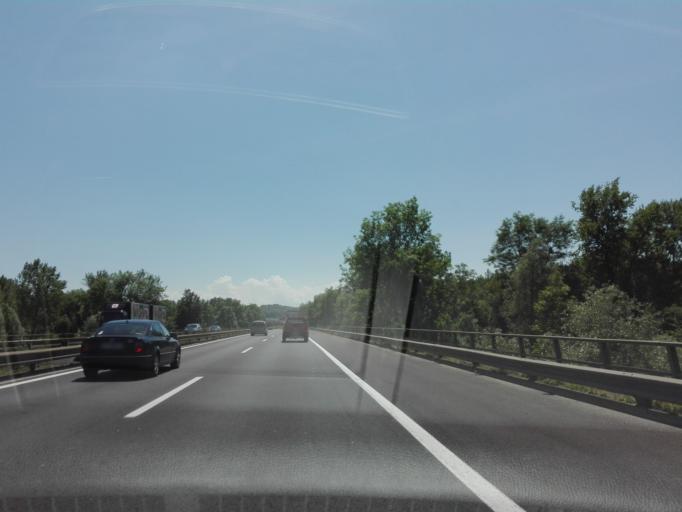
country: AT
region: Upper Austria
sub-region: Politischer Bezirk Linz-Land
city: Ansfelden
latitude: 48.2348
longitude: 14.2977
